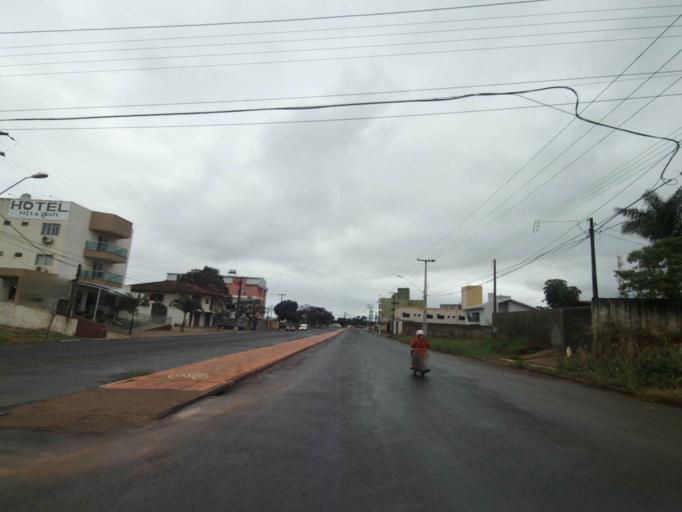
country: BR
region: Parana
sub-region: Foz Do Iguacu
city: Foz do Iguacu
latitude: -25.5176
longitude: -54.5616
